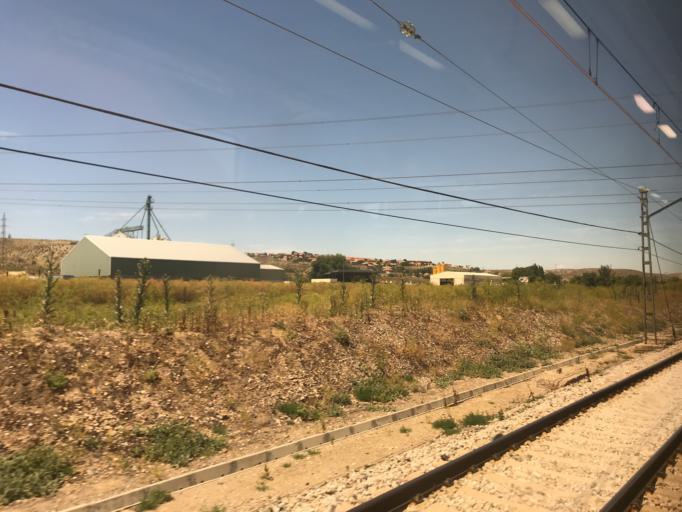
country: ES
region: Madrid
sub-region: Provincia de Madrid
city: Ciempozuelos
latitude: 40.0983
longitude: -3.6277
